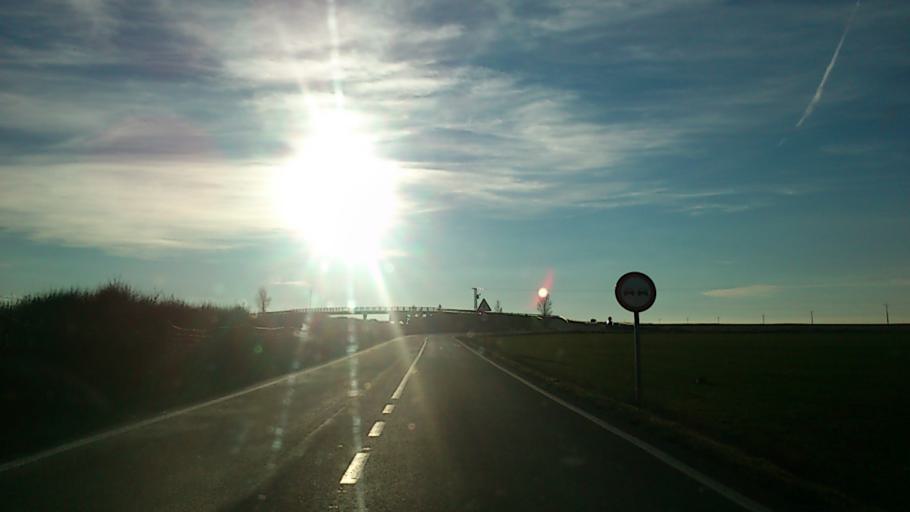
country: ES
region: Castille-La Mancha
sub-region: Provincia de Guadalajara
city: Almadrones
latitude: 40.8916
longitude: -2.7708
